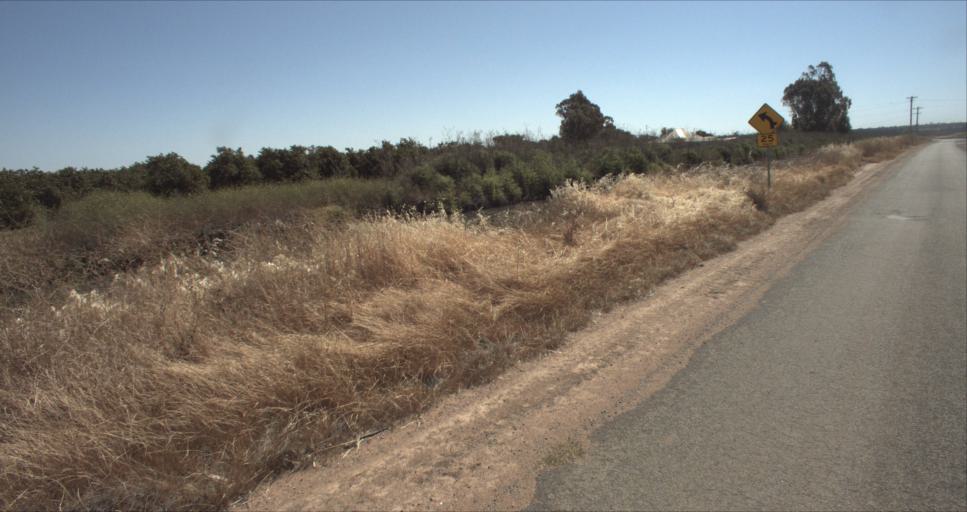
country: AU
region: New South Wales
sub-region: Leeton
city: Leeton
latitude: -34.4682
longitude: 146.4149
